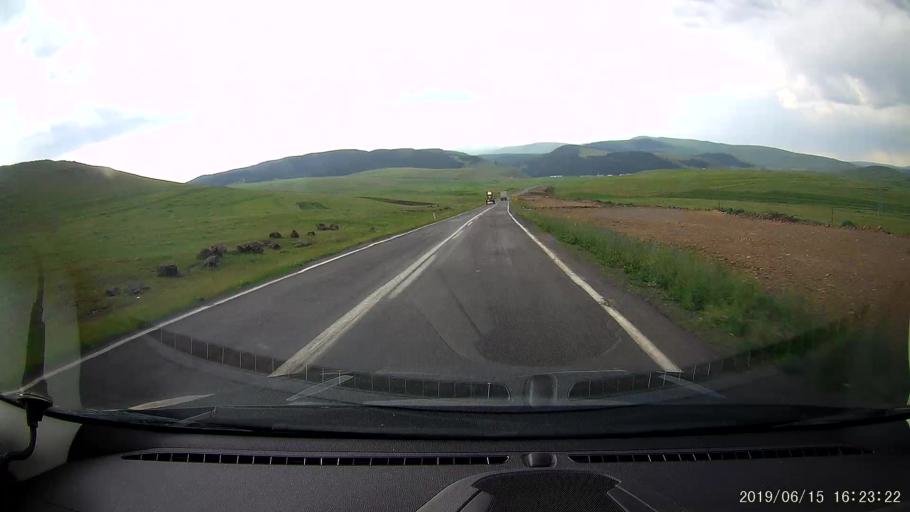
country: TR
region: Ardahan
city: Hanak
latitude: 41.1786
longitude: 42.8616
